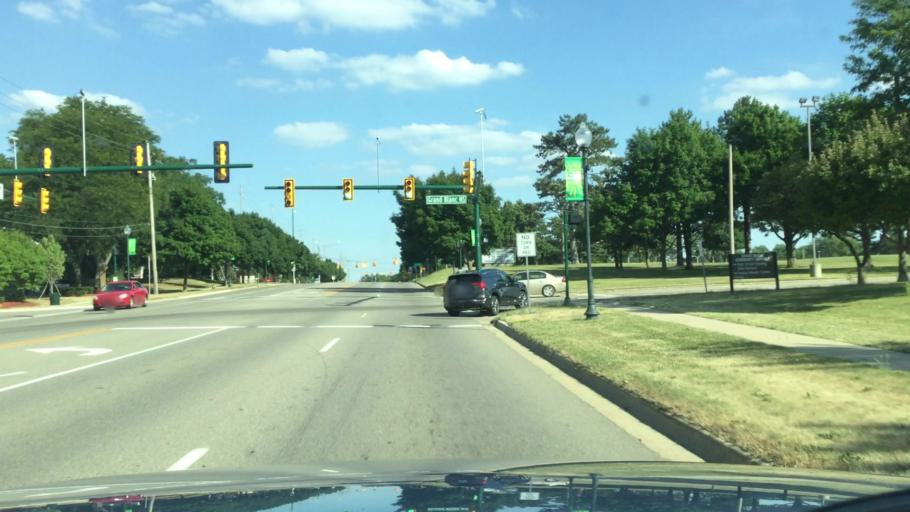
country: US
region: Michigan
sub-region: Genesee County
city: Grand Blanc
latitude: 42.9224
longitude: -83.6240
